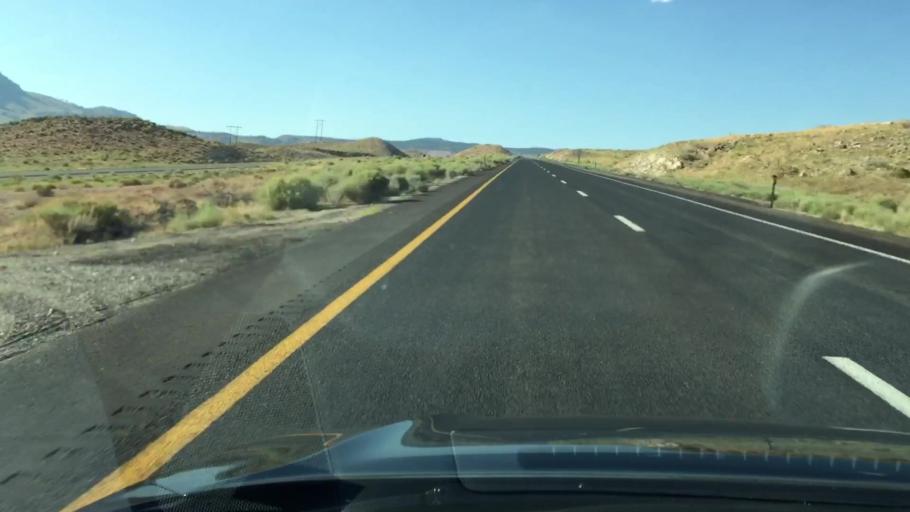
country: US
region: California
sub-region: Inyo County
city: West Bishop
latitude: 37.4571
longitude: -118.5753
